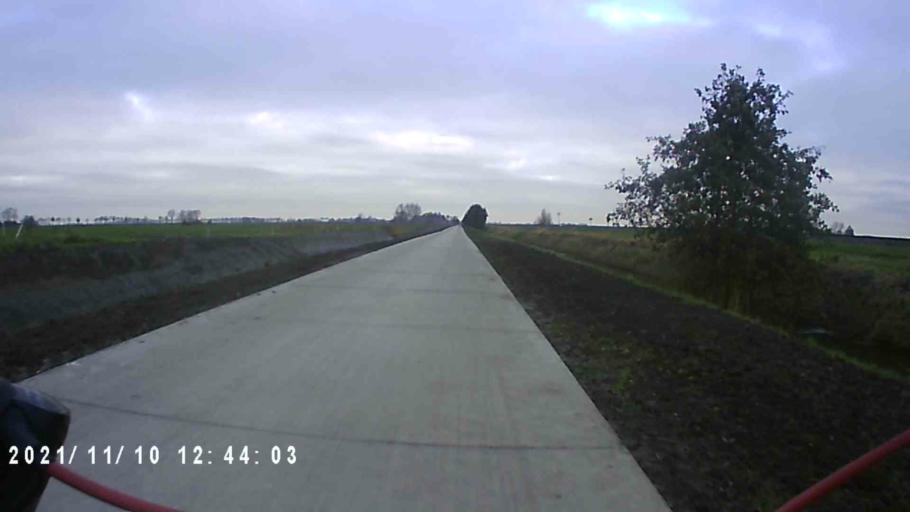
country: NL
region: Groningen
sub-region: Gemeente Groningen
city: Korrewegwijk
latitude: 53.2559
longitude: 6.5501
